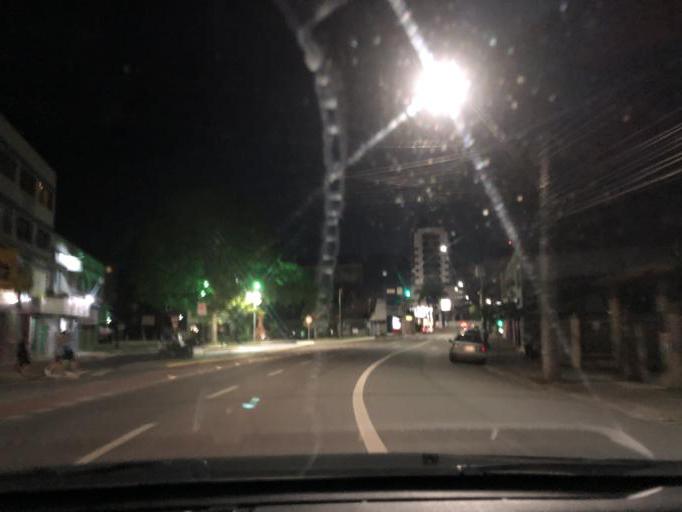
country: BR
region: Santa Catarina
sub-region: Jaragua Do Sul
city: Jaragua do Sul
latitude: -26.4906
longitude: -49.0829
